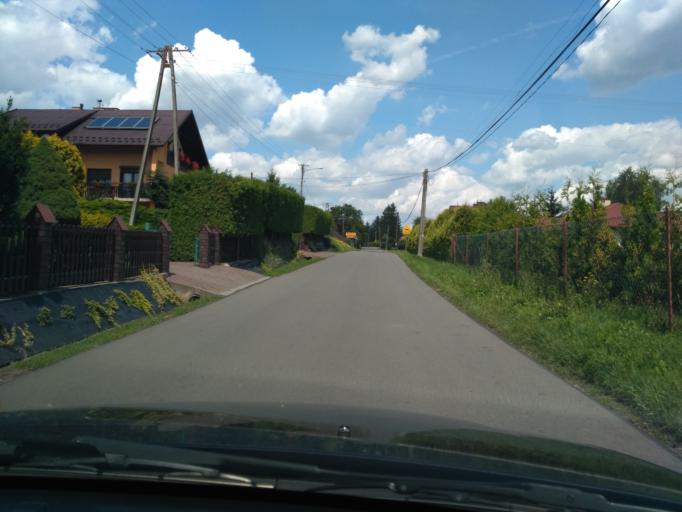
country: PL
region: Subcarpathian Voivodeship
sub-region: Powiat strzyzowski
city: Strzyzow
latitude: 49.8771
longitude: 21.7555
